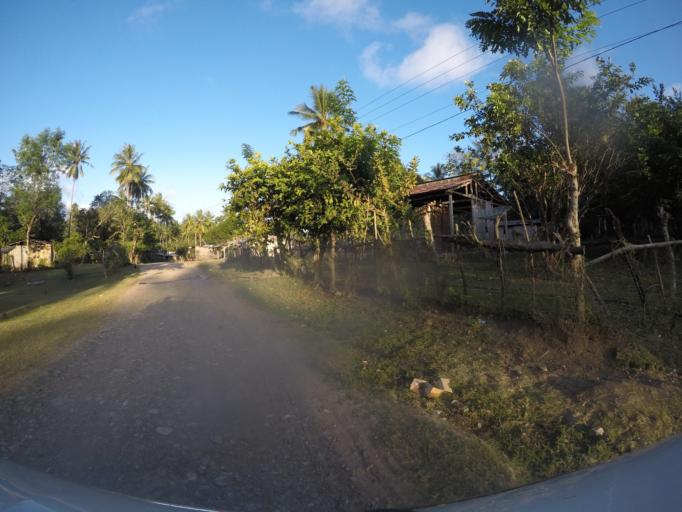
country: TL
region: Baucau
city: Venilale
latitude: -8.7329
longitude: 126.7102
